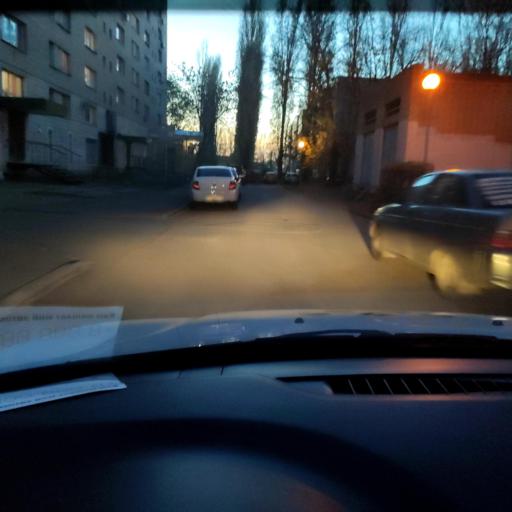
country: RU
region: Samara
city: Tol'yatti
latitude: 53.5221
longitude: 49.2631
